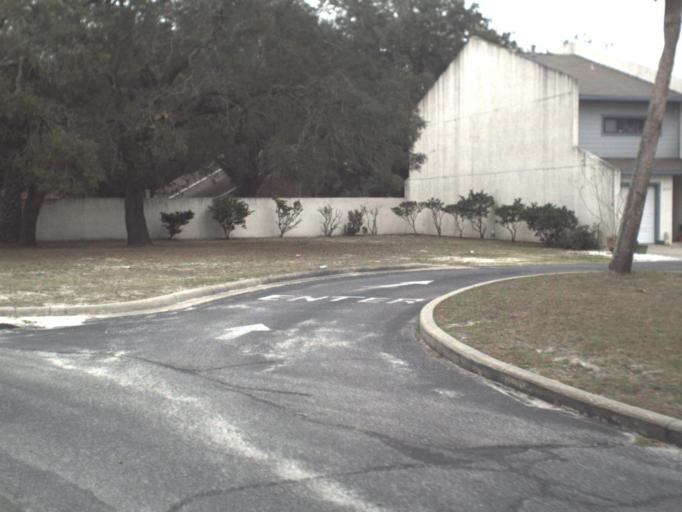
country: US
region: Florida
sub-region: Bay County
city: Parker
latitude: 30.1150
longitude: -85.5987
